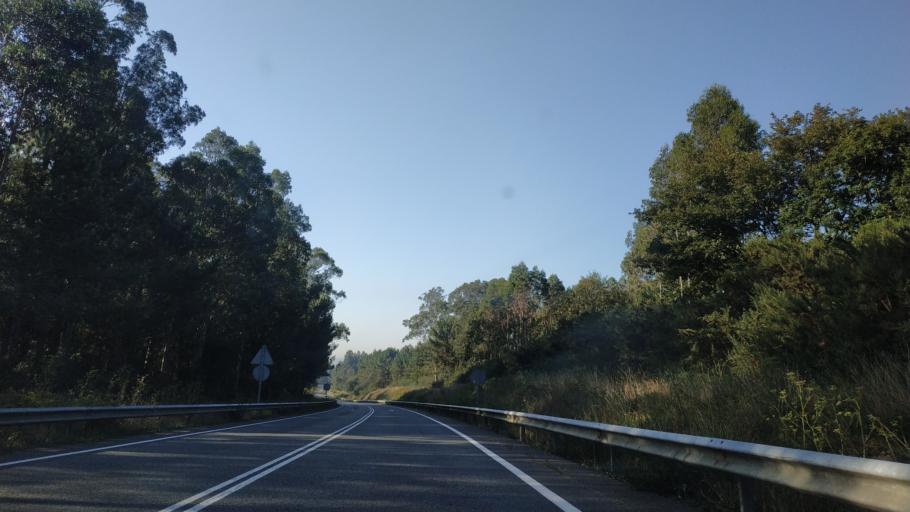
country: ES
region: Galicia
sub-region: Provincia da Coruna
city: Carballo
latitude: 43.2380
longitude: -8.6781
